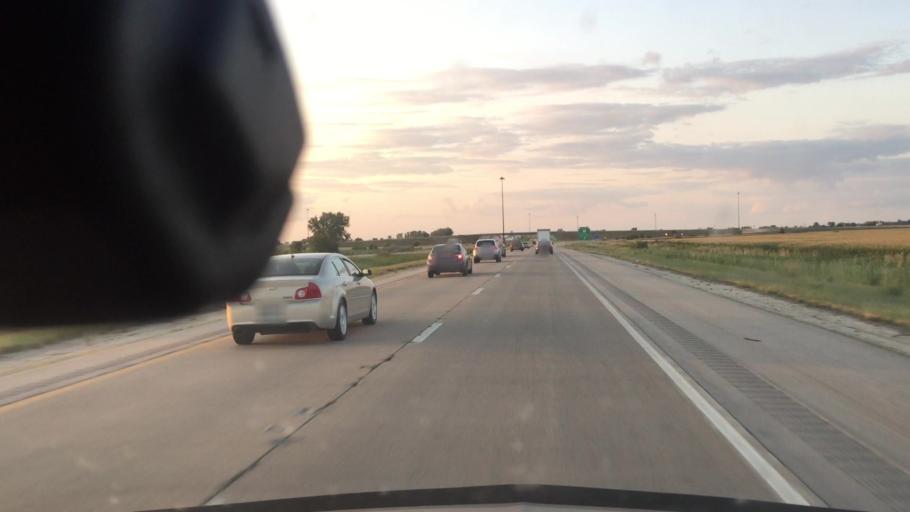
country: US
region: Illinois
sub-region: Livingston County
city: Dwight
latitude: 41.0860
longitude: -88.4516
